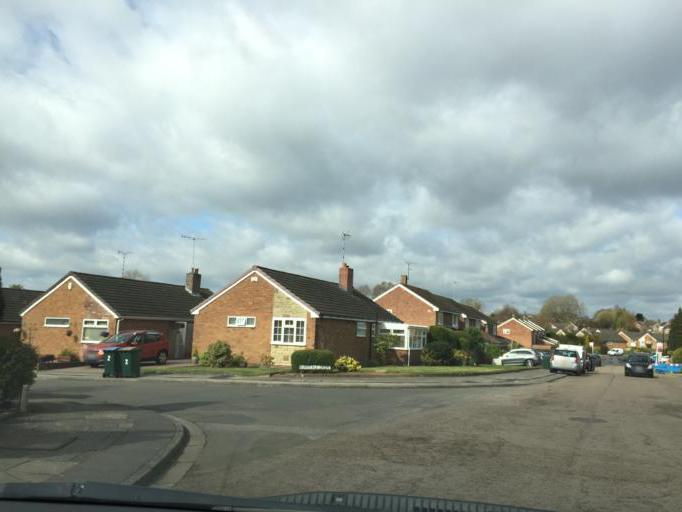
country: GB
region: England
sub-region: Coventry
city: Coventry
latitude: 52.3817
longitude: -1.5176
